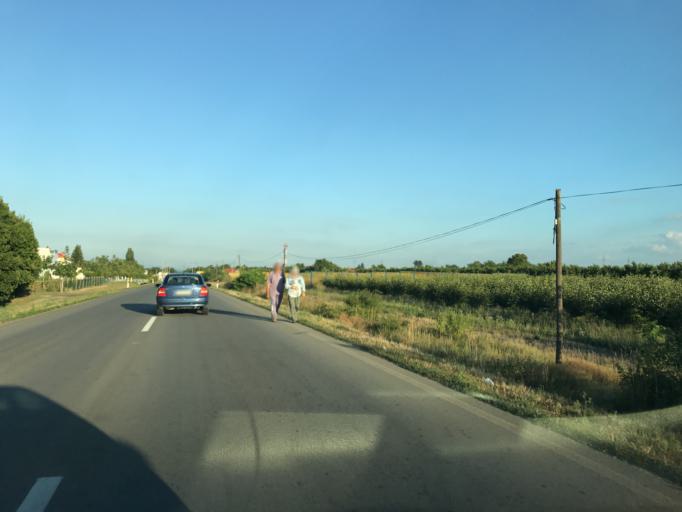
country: RS
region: Central Serbia
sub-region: Podunavski Okrug
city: Smederevo
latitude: 44.6177
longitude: 20.8960
